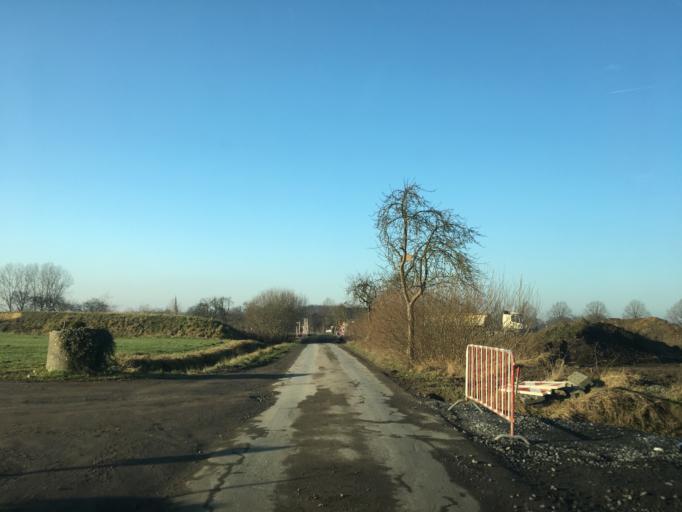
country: DE
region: North Rhine-Westphalia
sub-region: Regierungsbezirk Munster
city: Nordwalde
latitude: 52.0805
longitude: 7.4945
